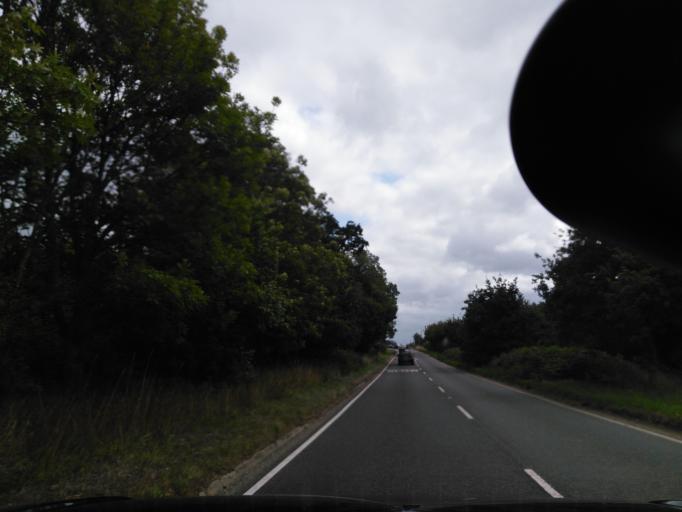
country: GB
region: England
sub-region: Dorset
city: Lytchett Matravers
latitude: 50.7381
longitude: -2.0937
